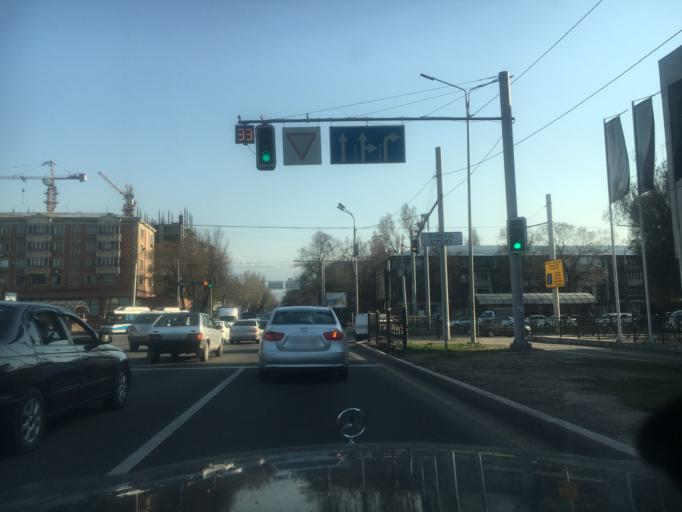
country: KZ
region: Almaty Qalasy
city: Almaty
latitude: 43.2710
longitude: 76.9446
